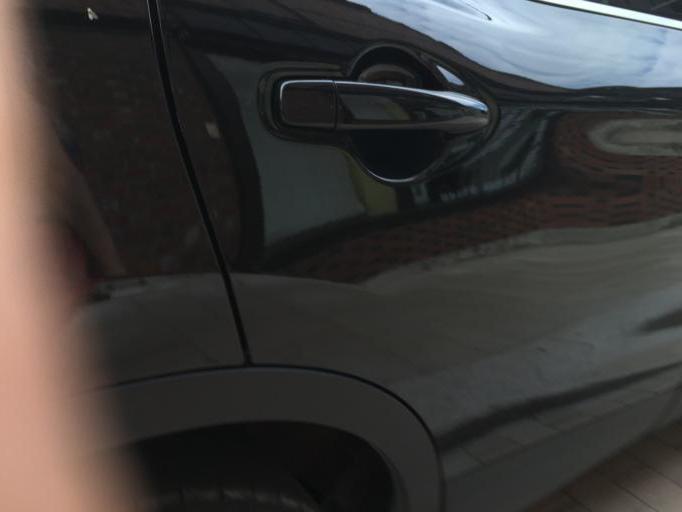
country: FR
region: Centre
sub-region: Departement du Cher
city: Aubigny-sur-Nere
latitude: 47.4875
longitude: 2.4384
